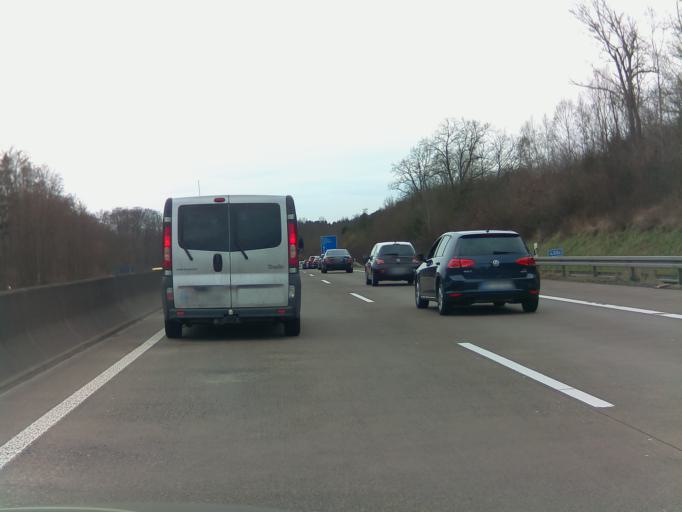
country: DE
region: Hesse
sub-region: Regierungsbezirk Giessen
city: Reiskirchen
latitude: 50.6124
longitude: 8.8481
